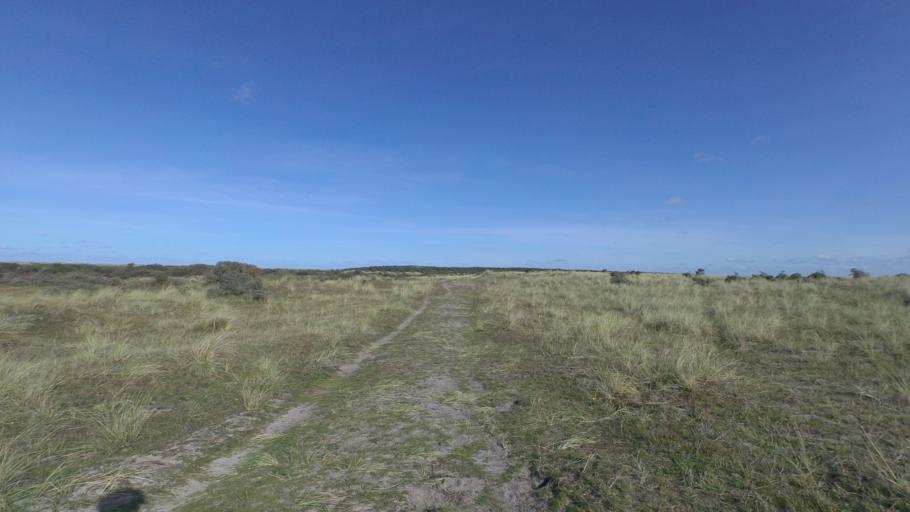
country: NL
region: Friesland
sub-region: Gemeente Ameland
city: Nes
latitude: 53.4499
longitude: 5.7396
